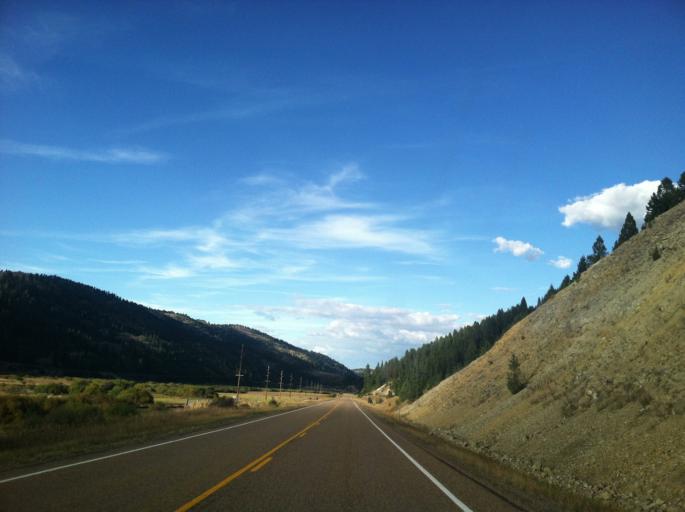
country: US
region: Montana
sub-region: Granite County
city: Philipsburg
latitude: 46.4039
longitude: -113.2953
